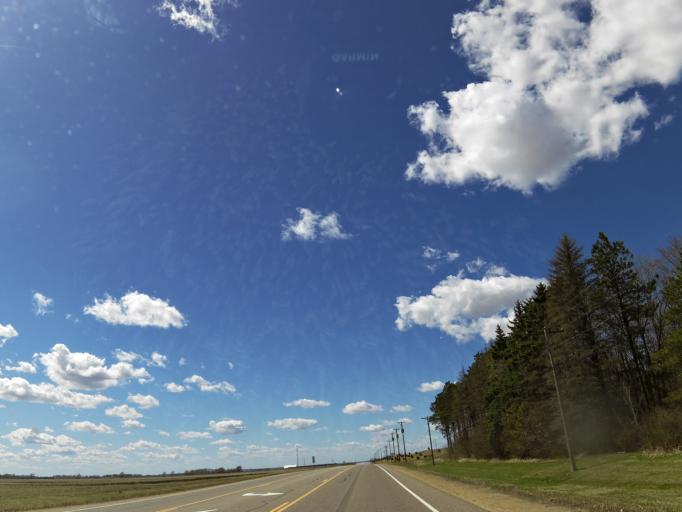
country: US
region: Minnesota
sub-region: Dakota County
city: Rosemount
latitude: 44.7175
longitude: -93.0982
